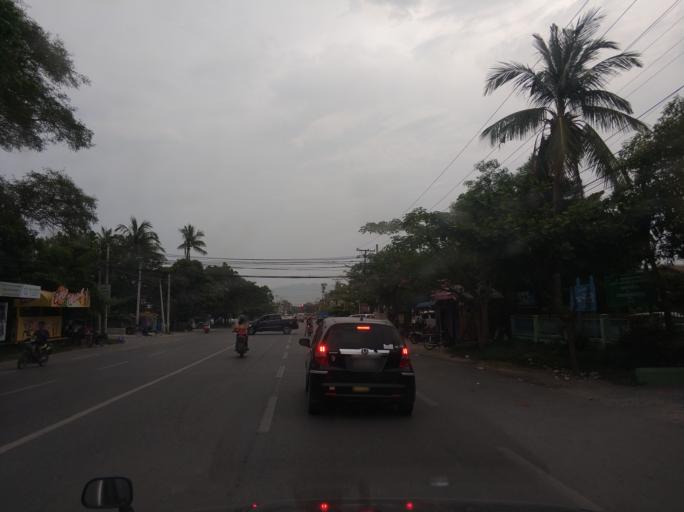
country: MM
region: Mandalay
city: Mandalay
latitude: 21.9755
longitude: 96.1109
